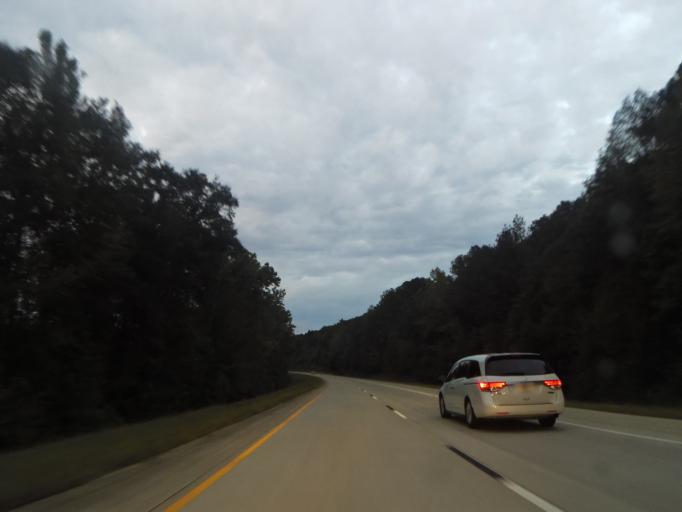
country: US
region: Alabama
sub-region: Etowah County
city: Attalla
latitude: 34.0511
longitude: -86.0457
